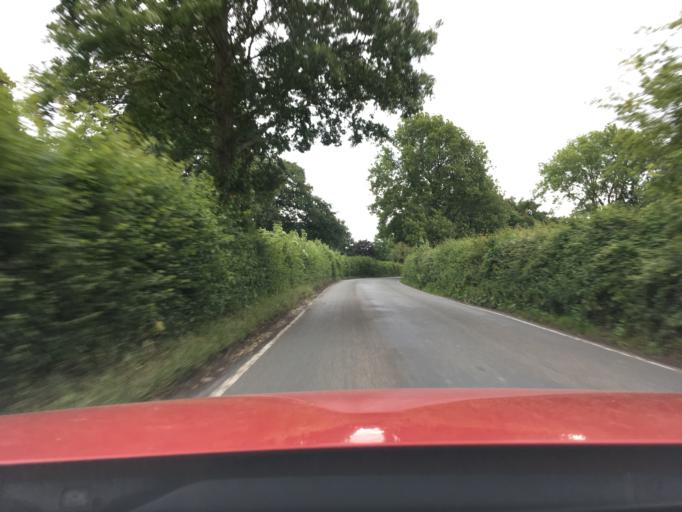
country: GB
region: England
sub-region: Gloucestershire
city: Stonehouse
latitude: 51.7757
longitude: -2.3721
